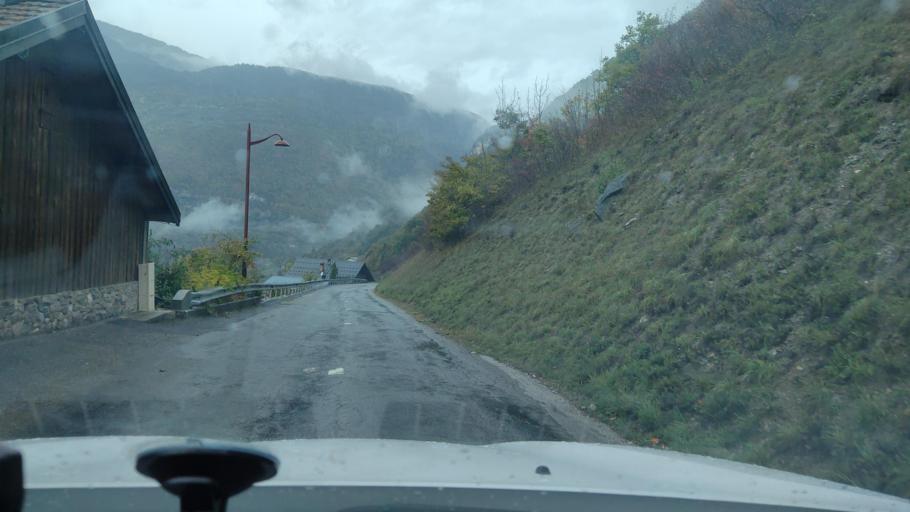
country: FR
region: Rhone-Alpes
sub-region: Departement de la Savoie
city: Salins-les-Thermes
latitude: 45.4631
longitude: 6.5504
